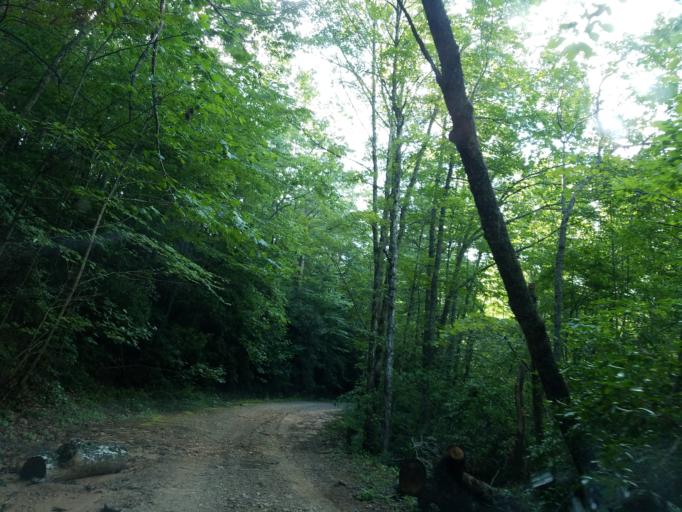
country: US
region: Georgia
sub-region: Dawson County
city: Dawsonville
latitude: 34.6252
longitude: -84.2364
